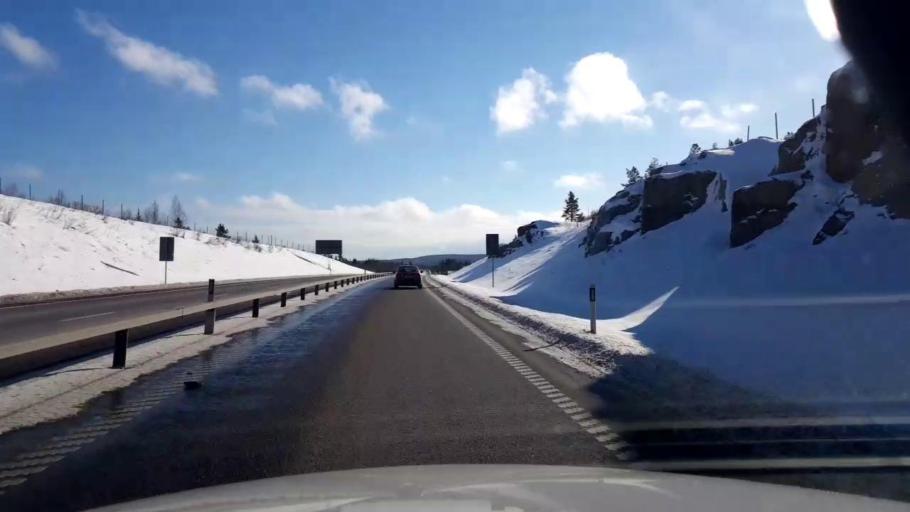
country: SE
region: Vaesternorrland
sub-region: Sundsvalls Kommun
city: Njurundabommen
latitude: 62.2593
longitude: 17.3655
